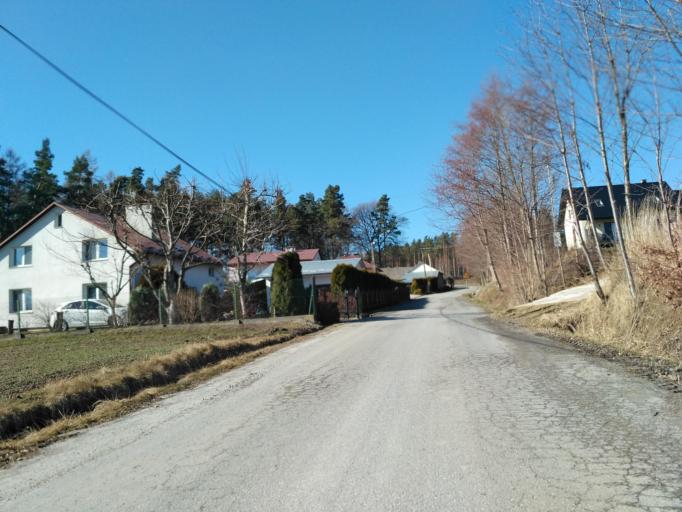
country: PL
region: Subcarpathian Voivodeship
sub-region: Powiat rzeszowski
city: Lutoryz
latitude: 49.9631
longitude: 21.8905
